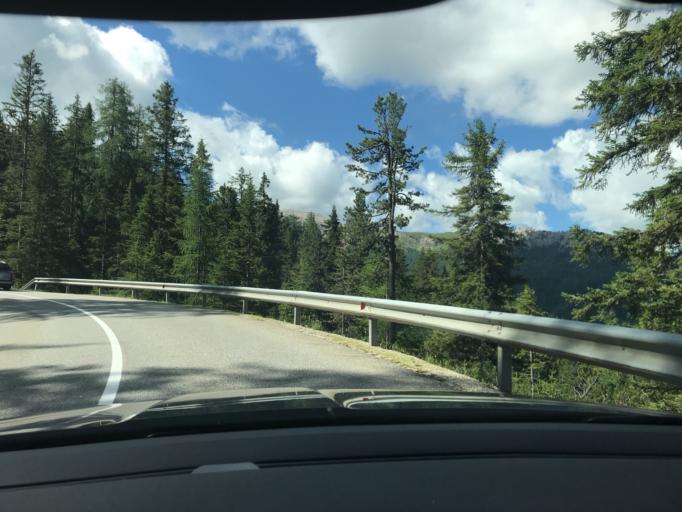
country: IT
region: Veneto
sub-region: Provincia di Belluno
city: Livinallongo del Col di Lana
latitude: 46.5535
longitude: 11.9775
